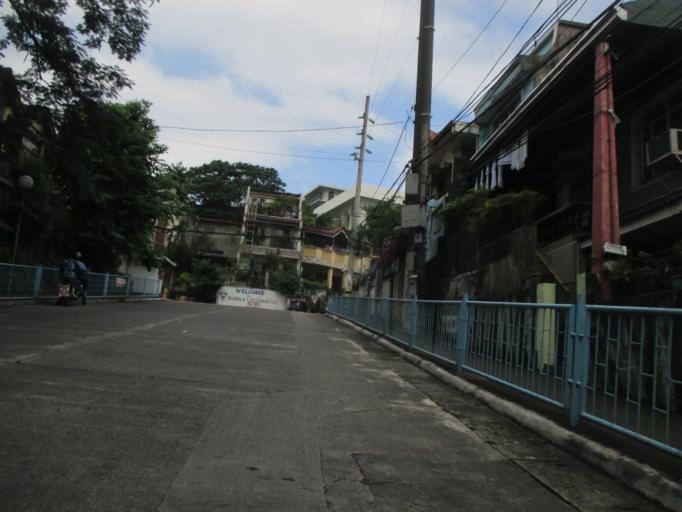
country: PH
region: Metro Manila
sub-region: Marikina
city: Calumpang
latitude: 14.6348
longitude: 121.0826
